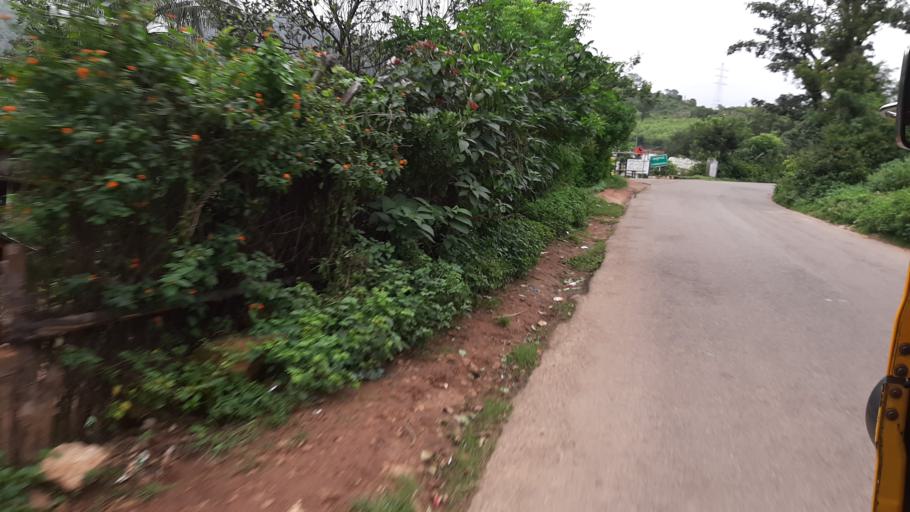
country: IN
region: Andhra Pradesh
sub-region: Vizianagaram District
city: Salur
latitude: 18.2397
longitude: 82.9991
